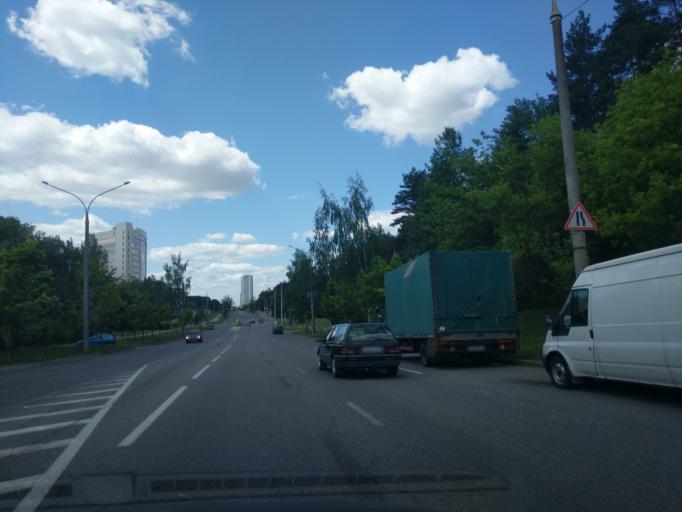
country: BY
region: Minsk
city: Borovlyany
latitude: 53.9241
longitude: 27.6702
